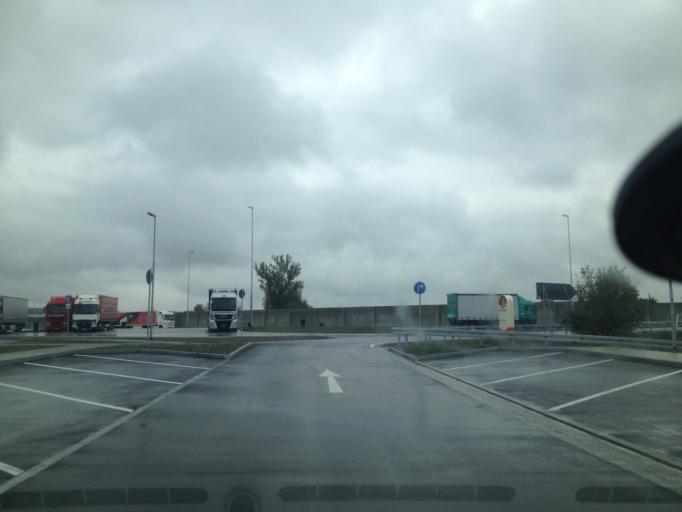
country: DE
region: Bavaria
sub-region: Swabia
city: Rofingen
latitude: 48.4136
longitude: 10.4256
